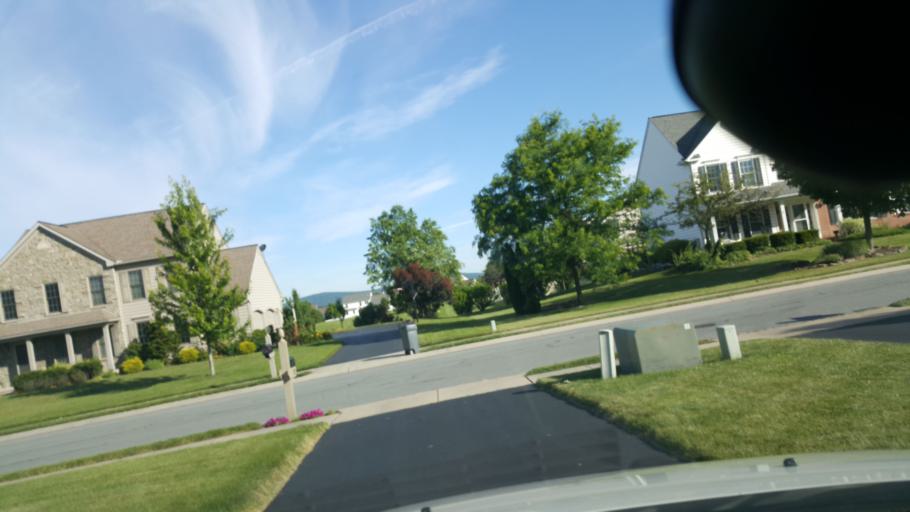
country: US
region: Pennsylvania
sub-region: York County
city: Shiloh
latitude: 39.9916
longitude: -76.7803
